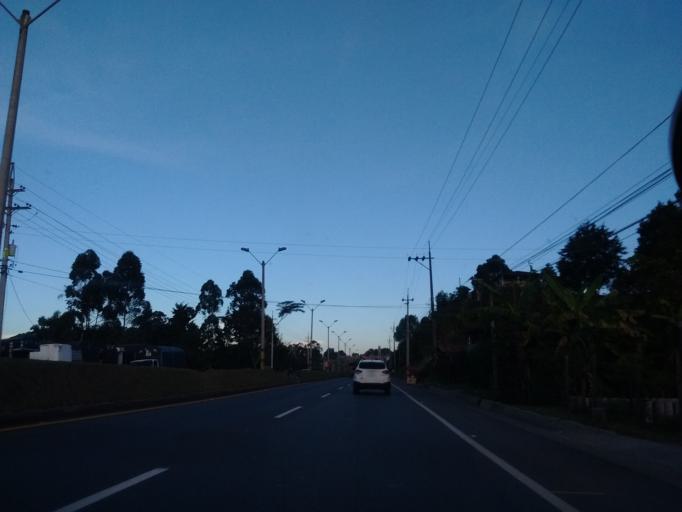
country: CO
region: Antioquia
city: Rionegro
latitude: 6.1829
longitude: -75.3731
